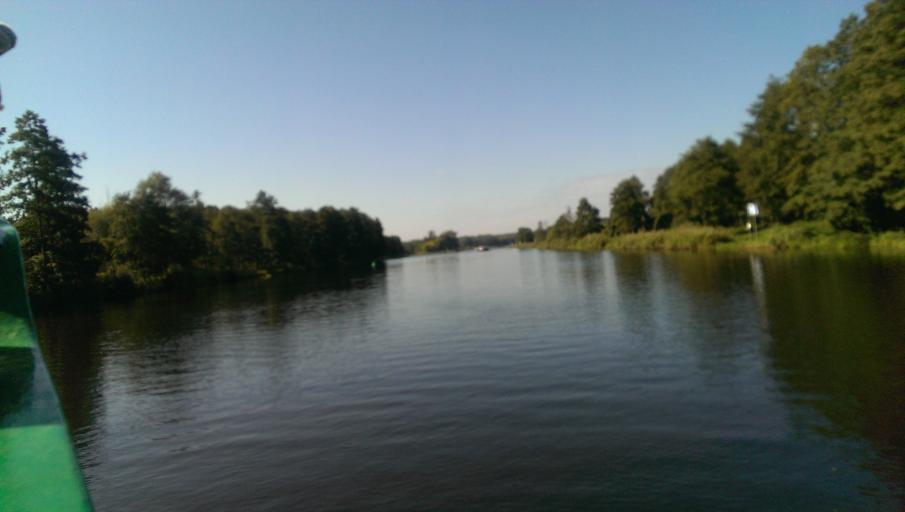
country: DE
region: Brandenburg
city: Liepe
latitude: 52.8546
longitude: 13.9654
